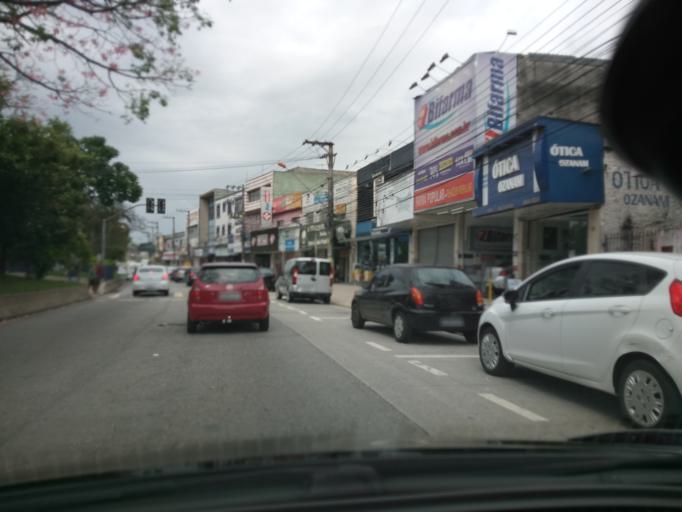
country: BR
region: Sao Paulo
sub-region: Sao Bernardo Do Campo
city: Sao Bernardo do Campo
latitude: -23.6919
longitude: -46.5815
